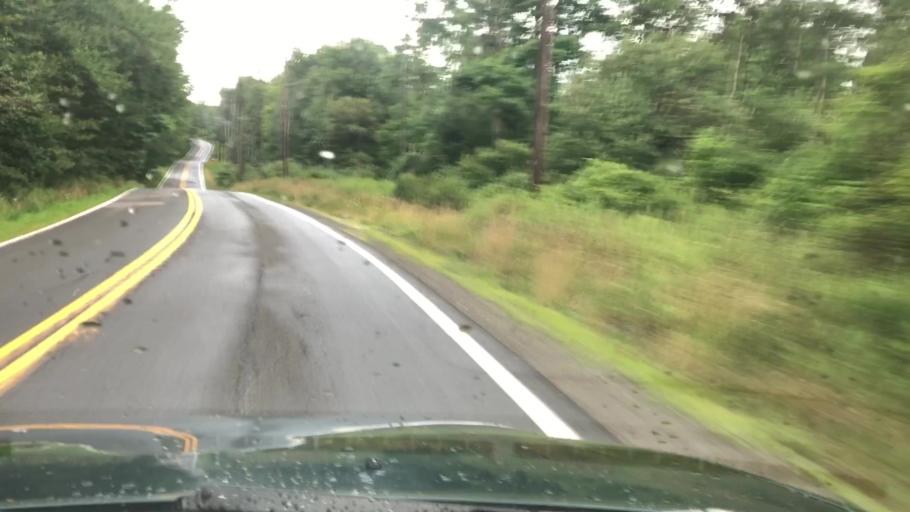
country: US
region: Pennsylvania
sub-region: Monroe County
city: Mountainhome
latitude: 41.2869
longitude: -75.2348
